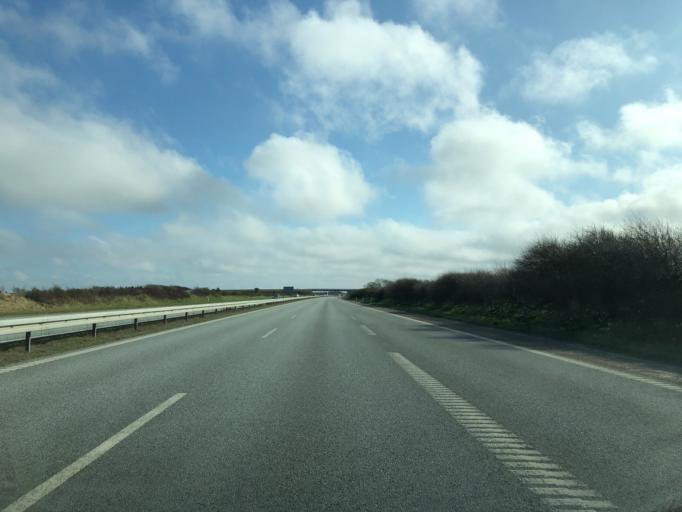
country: DK
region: North Denmark
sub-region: Hjorring Kommune
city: Hjorring
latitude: 57.4525
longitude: 10.0439
